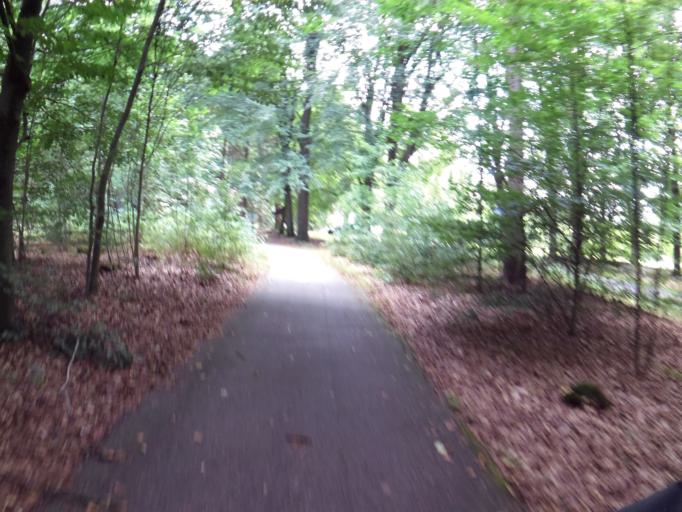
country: NL
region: Drenthe
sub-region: Gemeente Borger-Odoorn
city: Borger
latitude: 52.9620
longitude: 6.7575
